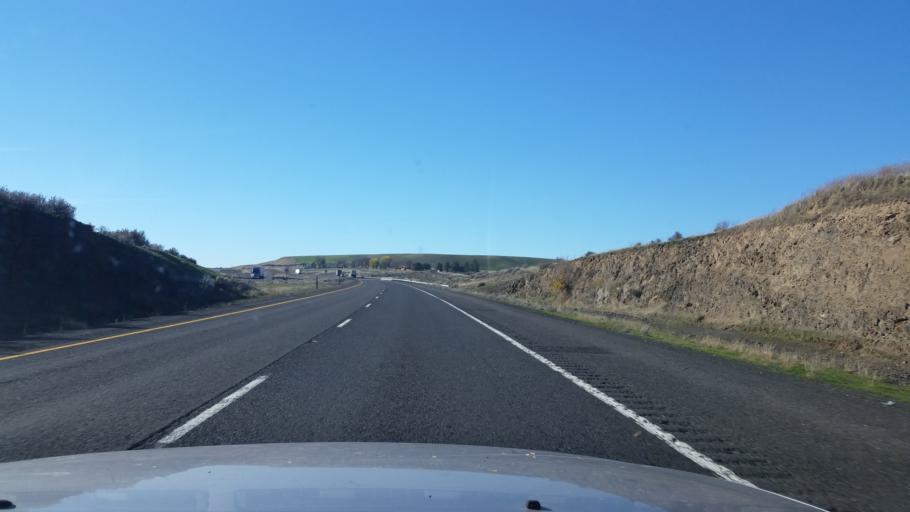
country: US
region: Washington
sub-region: Lincoln County
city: Davenport
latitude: 47.2995
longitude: -118.0222
